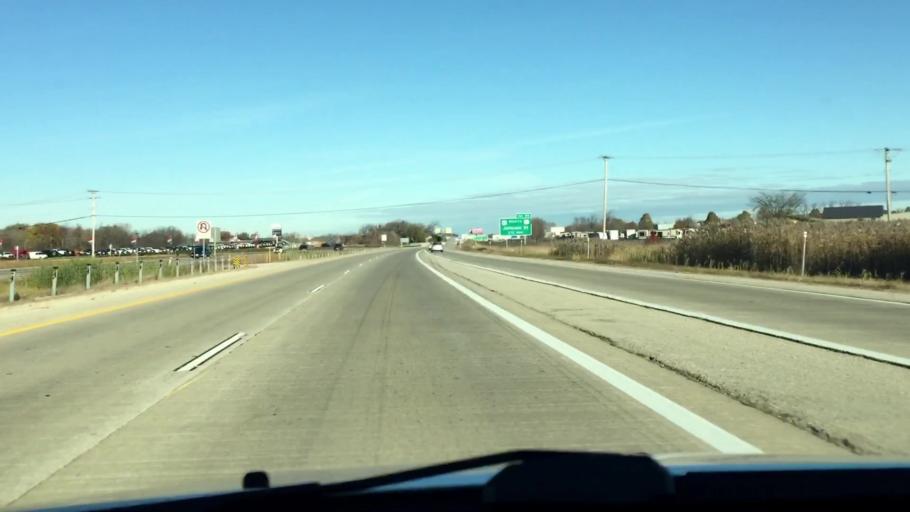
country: US
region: Wisconsin
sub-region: Fond du Lac County
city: Fond du Lac
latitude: 43.7616
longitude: -88.4775
